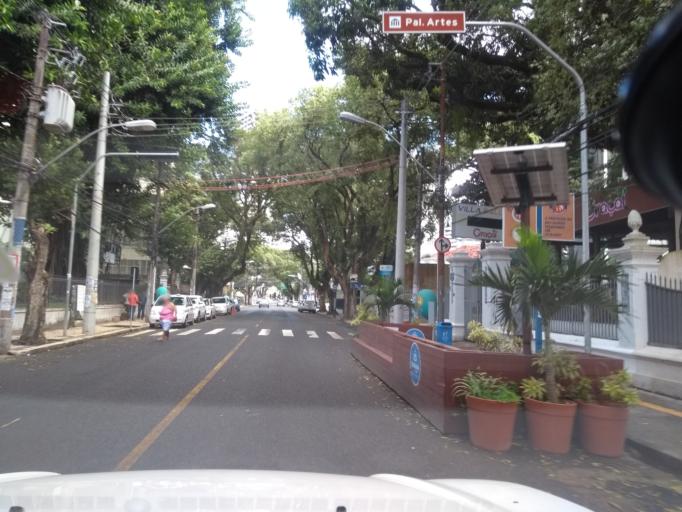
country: BR
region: Bahia
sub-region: Salvador
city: Salvador
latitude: -12.9977
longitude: -38.5252
